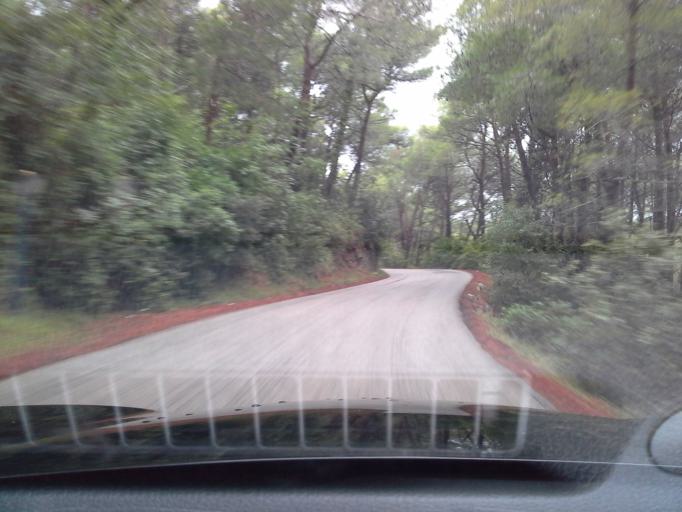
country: HR
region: Primorsko-Goranska
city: Mali Losinj
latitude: 44.5264
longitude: 14.4855
